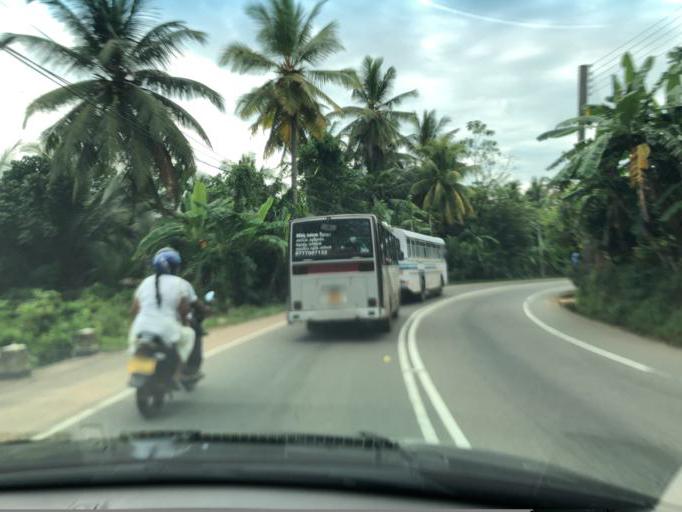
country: LK
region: Western
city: Beruwala
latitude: 6.5440
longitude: 80.0375
